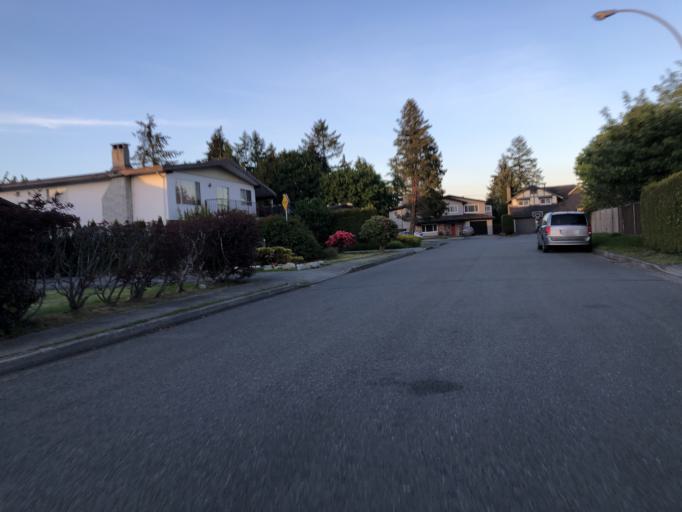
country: CA
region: British Columbia
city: Richmond
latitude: 49.1398
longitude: -123.1166
